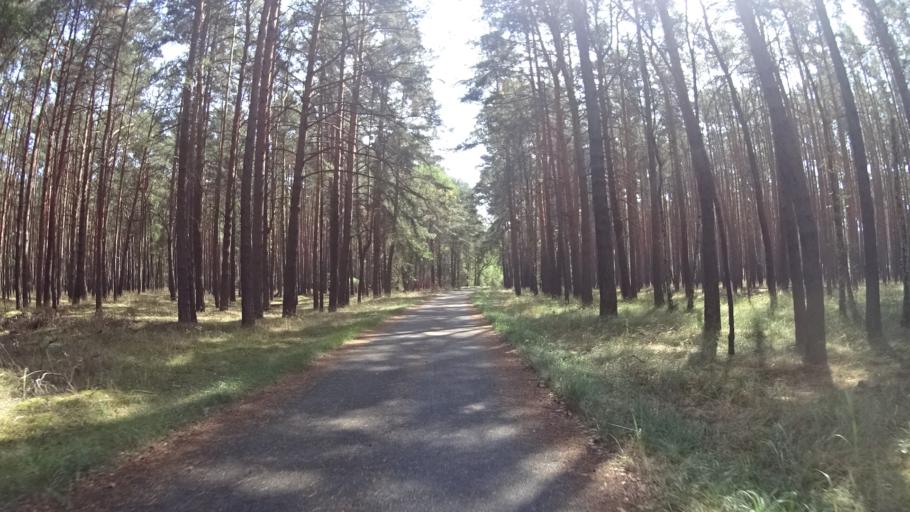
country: DE
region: Brandenburg
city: Briesen
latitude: 51.8056
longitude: 14.2794
